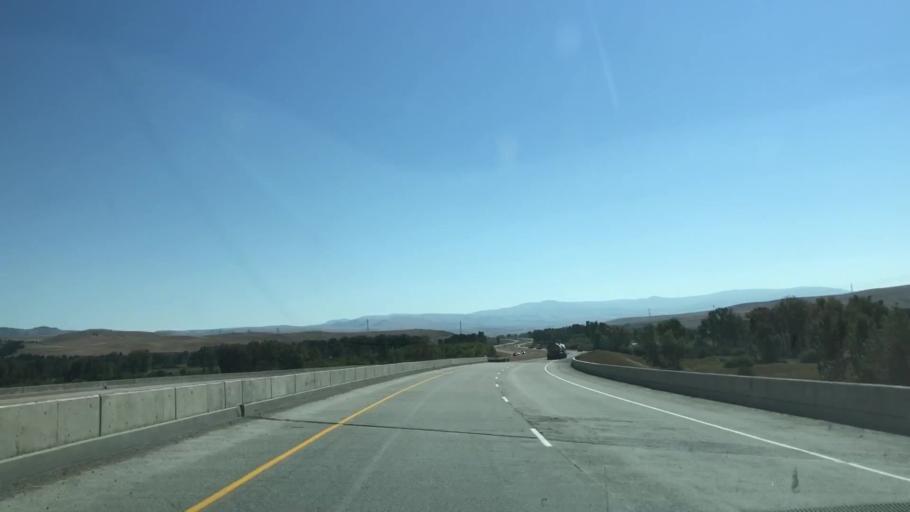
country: US
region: Montana
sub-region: Powell County
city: Deer Lodge
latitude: 46.5233
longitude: -112.8076
